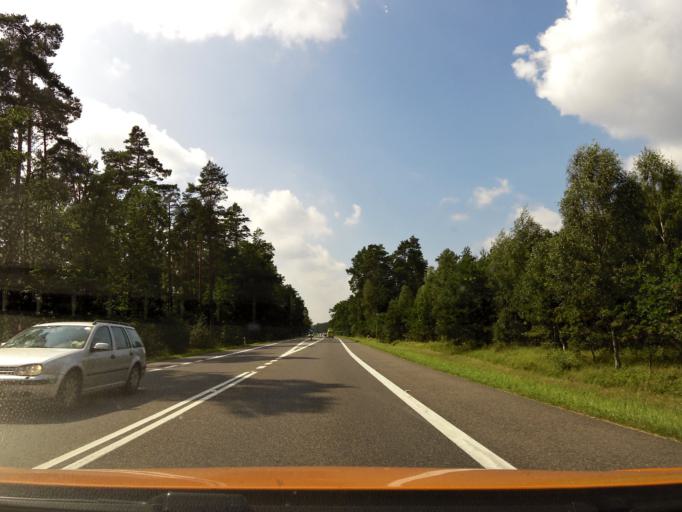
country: PL
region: West Pomeranian Voivodeship
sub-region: Powiat goleniowski
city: Goleniow
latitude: 53.6014
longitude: 14.8879
